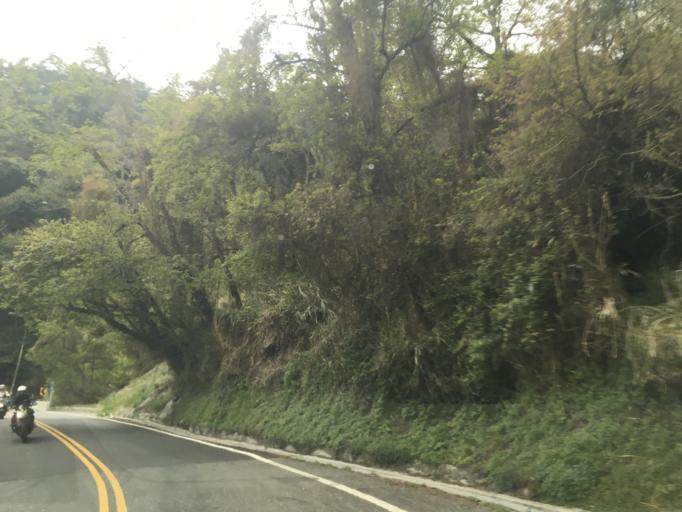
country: TW
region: Taiwan
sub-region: Hualien
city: Hualian
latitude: 24.1862
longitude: 121.3263
